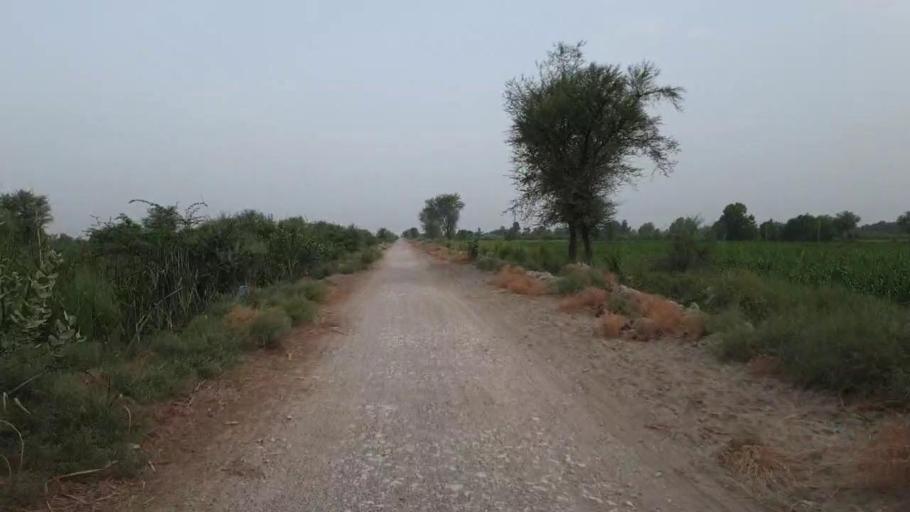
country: PK
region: Sindh
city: Daur
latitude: 26.4216
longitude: 68.2251
